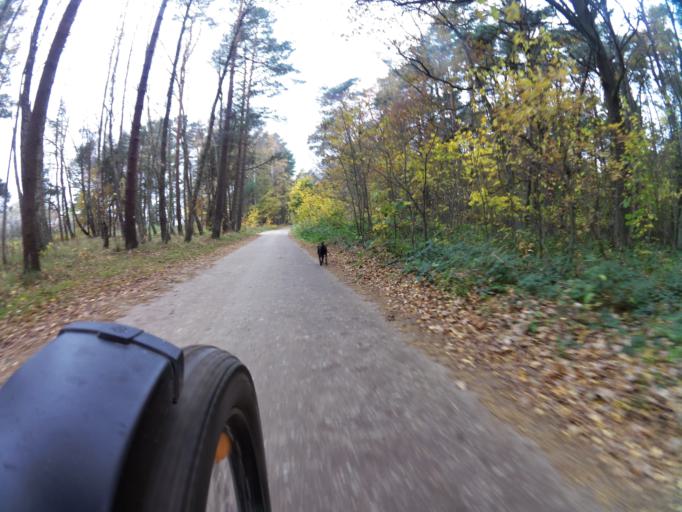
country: PL
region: Pomeranian Voivodeship
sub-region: Powiat pucki
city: Krokowa
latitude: 54.8295
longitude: 18.1380
